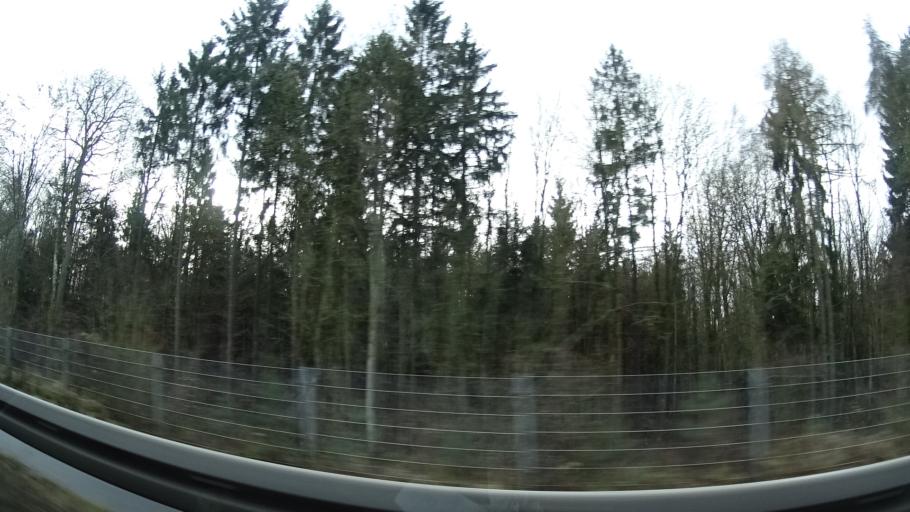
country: DE
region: Hesse
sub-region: Regierungsbezirk Giessen
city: Lich
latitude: 50.5293
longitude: 8.7821
